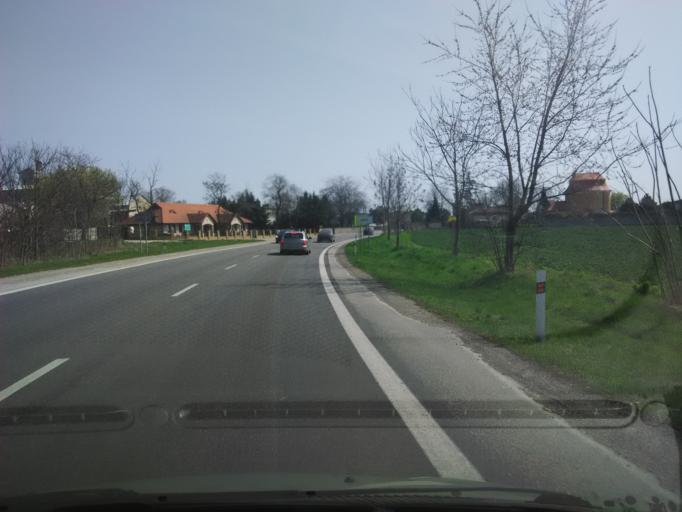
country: SK
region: Nitriansky
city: Sellye
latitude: 48.1346
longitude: 18.0217
